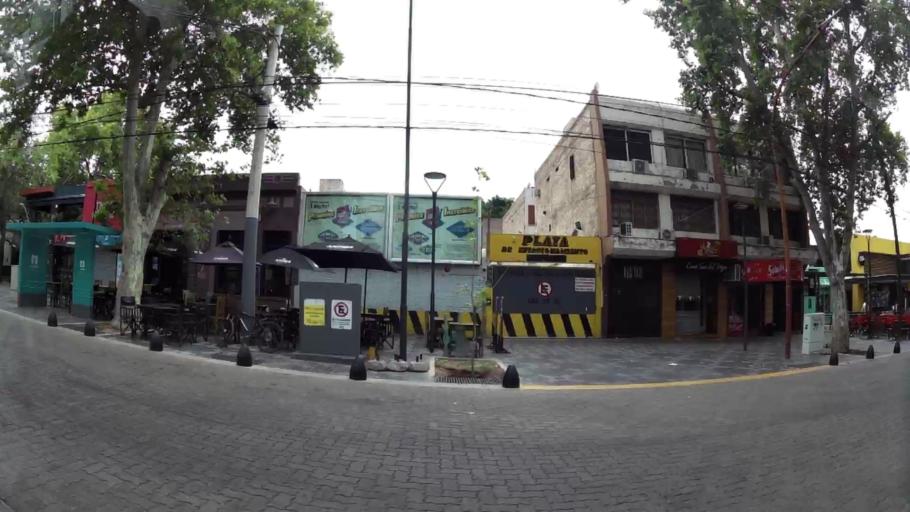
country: AR
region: Mendoza
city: Mendoza
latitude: -32.8924
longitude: -68.8545
